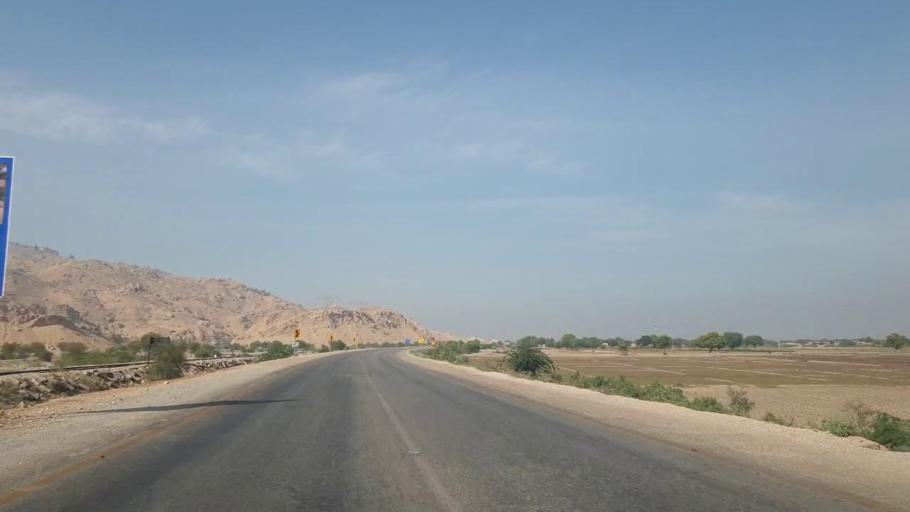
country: PK
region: Sindh
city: Sehwan
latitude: 26.2852
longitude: 67.8950
